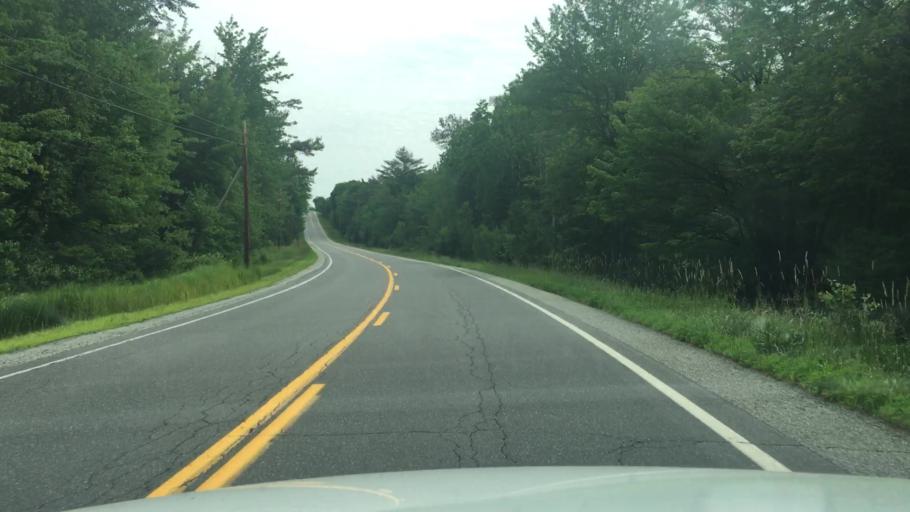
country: US
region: Maine
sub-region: Waldo County
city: Burnham
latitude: 44.6137
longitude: -69.4250
